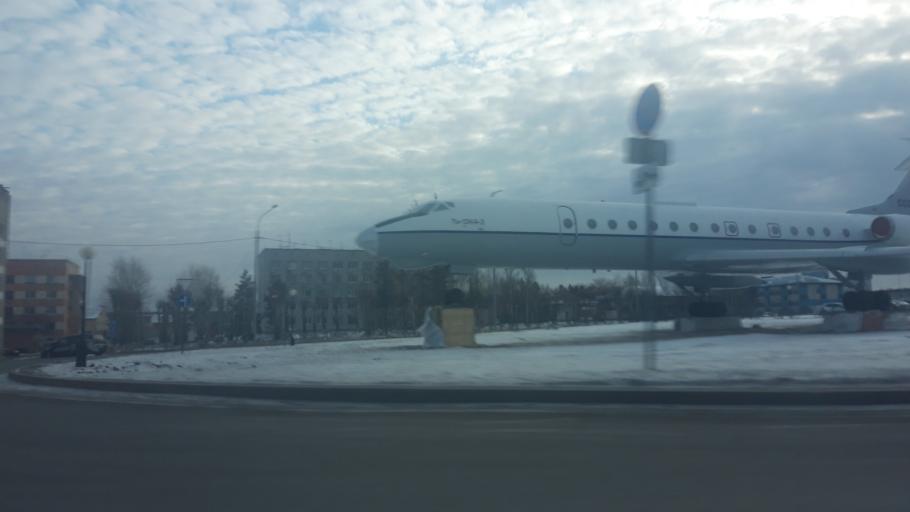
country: RU
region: Tjumen
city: Moskovskiy
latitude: 57.1833
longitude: 65.3516
